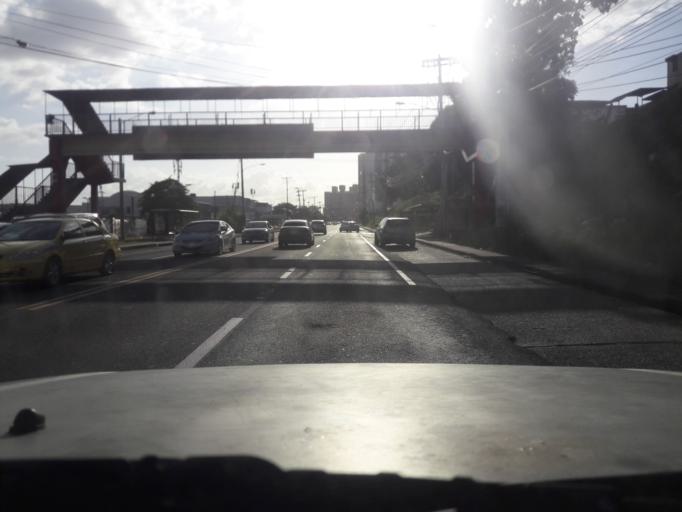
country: PA
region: Panama
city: San Miguelito
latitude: 9.0276
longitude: -79.4809
